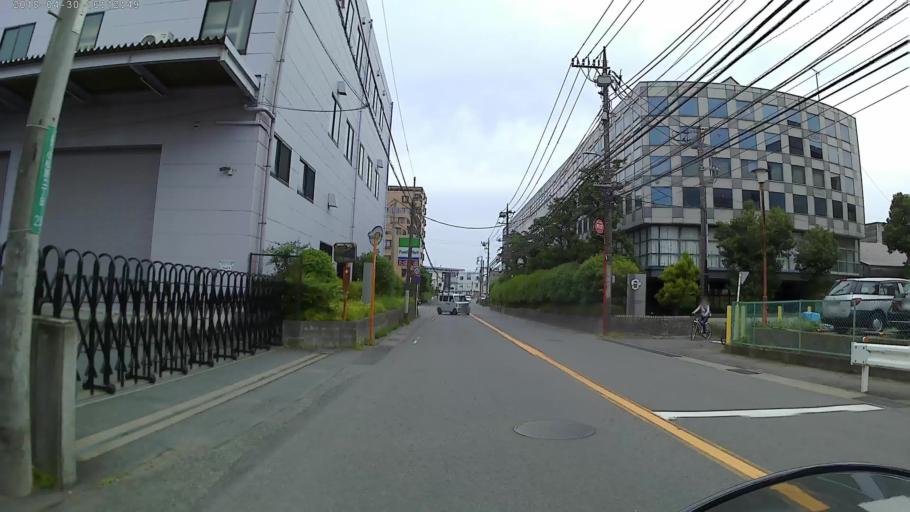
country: JP
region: Kanagawa
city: Minami-rinkan
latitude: 35.4936
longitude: 139.4305
